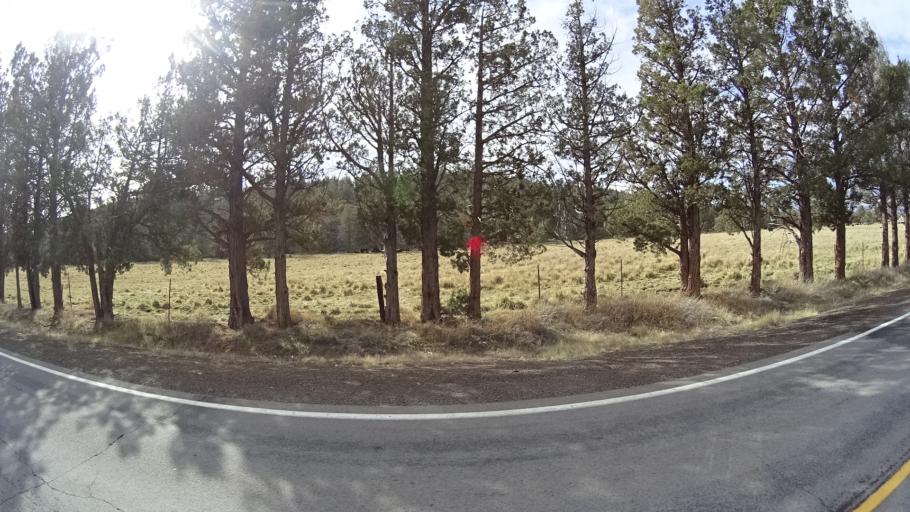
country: US
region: California
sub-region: Siskiyou County
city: Weed
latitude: 41.5782
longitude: -122.3968
